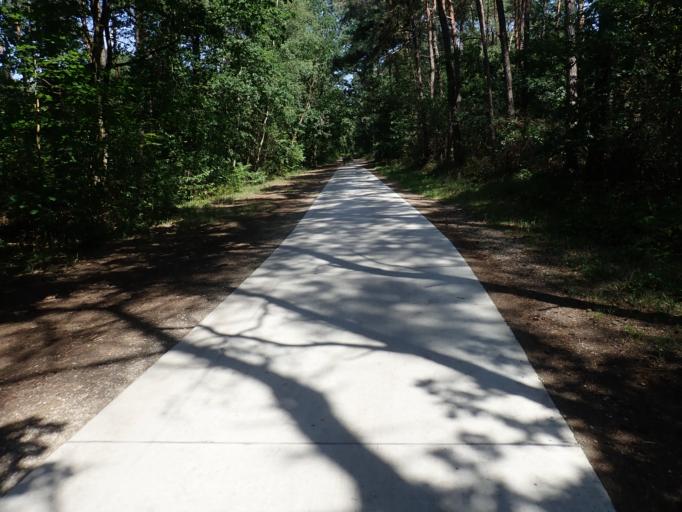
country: BE
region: Flanders
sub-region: Provincie Antwerpen
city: Zandhoven
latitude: 51.2274
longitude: 4.6247
